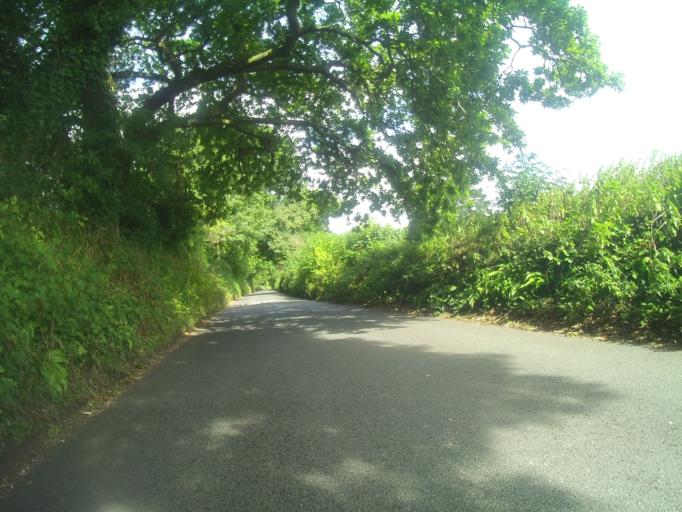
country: GB
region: England
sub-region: Devon
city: Totnes
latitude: 50.4394
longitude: -3.7047
